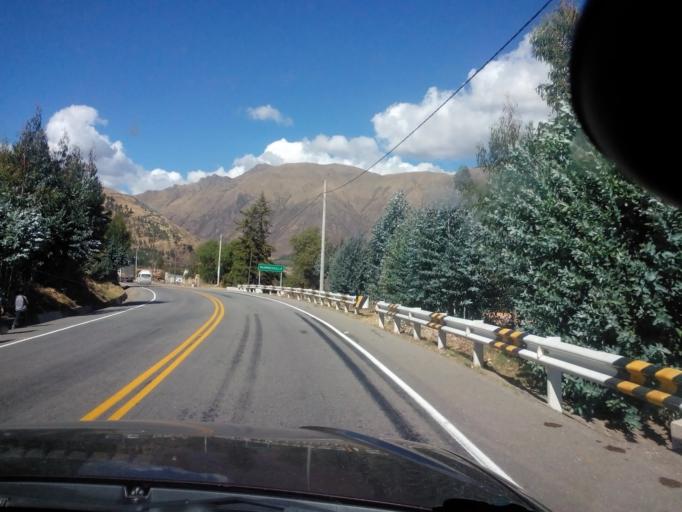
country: PE
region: Cusco
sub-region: Provincia de Quispicanchis
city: Urcos
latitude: -13.7071
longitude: -71.5974
